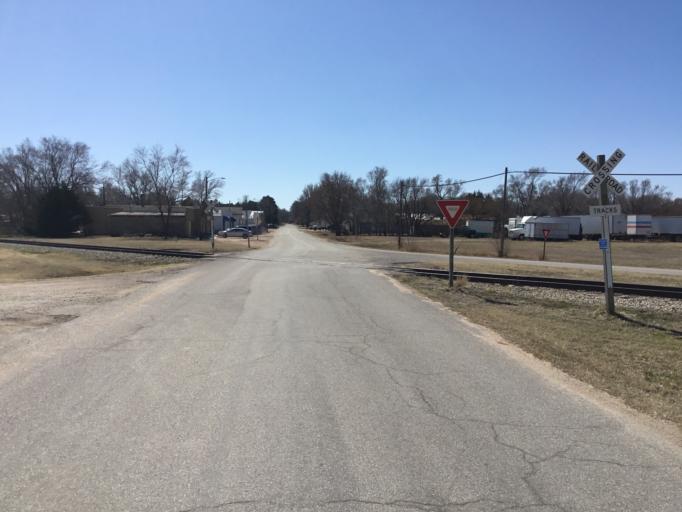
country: US
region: Kansas
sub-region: Sedgwick County
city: Maize
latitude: 37.7804
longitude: -97.4687
